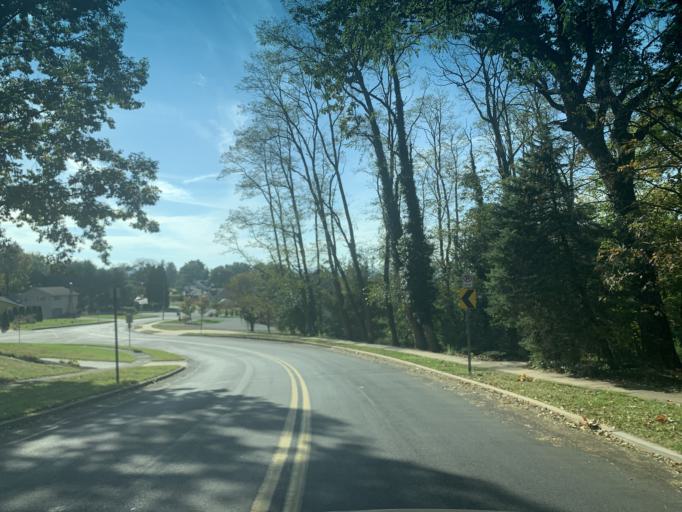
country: US
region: Pennsylvania
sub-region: Berks County
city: West Lawn
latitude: 40.3337
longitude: -75.9934
